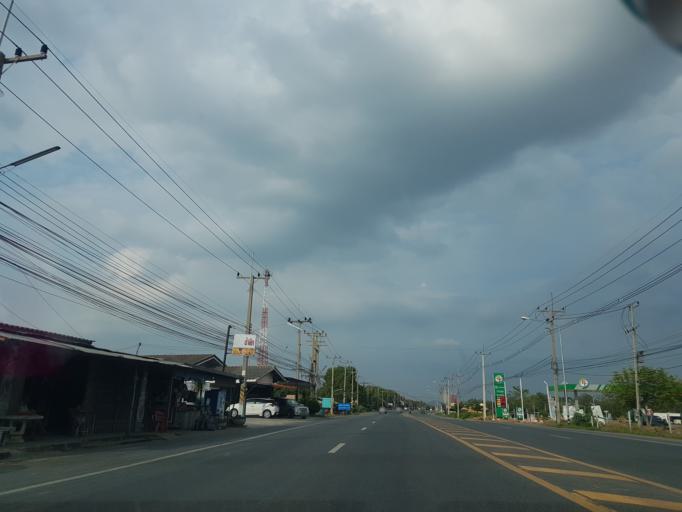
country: TH
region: Sara Buri
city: Phra Phutthabat
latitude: 14.6889
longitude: 100.7763
